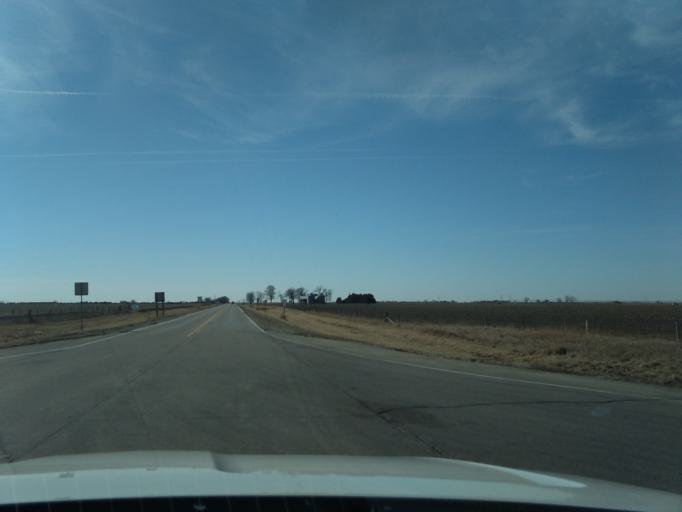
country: US
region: Nebraska
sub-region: Saline County
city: Friend
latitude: 40.8202
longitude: -97.2920
